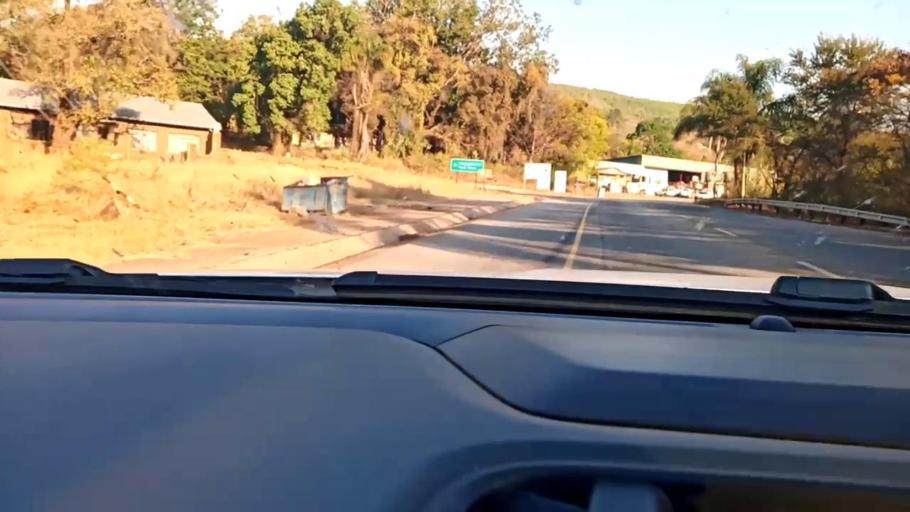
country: ZA
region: Limpopo
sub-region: Mopani District Municipality
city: Duiwelskloof
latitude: -23.6916
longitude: 30.1463
